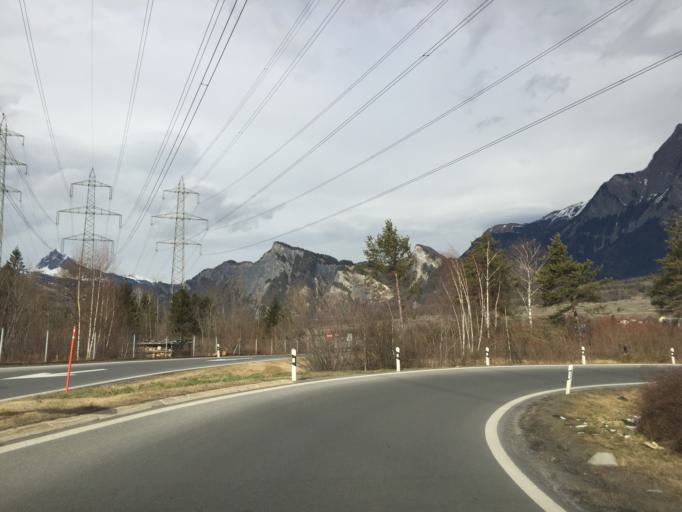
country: CH
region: Grisons
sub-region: Landquart District
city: Maienfeld
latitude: 47.0021
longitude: 9.5195
